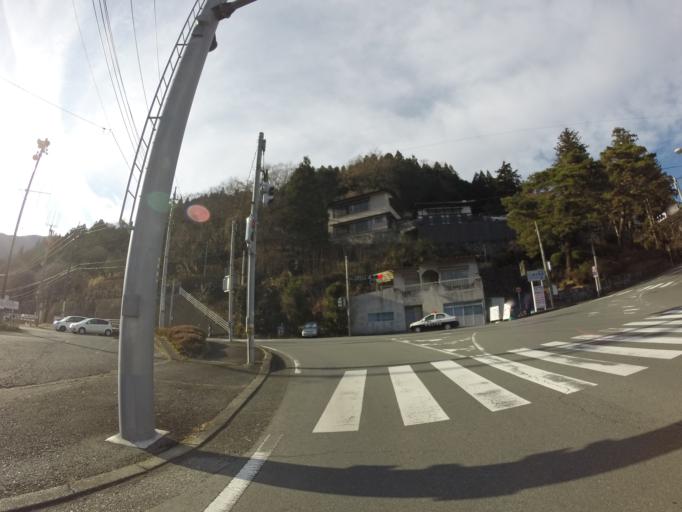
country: JP
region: Shizuoka
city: Fujinomiya
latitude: 35.3683
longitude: 138.4267
